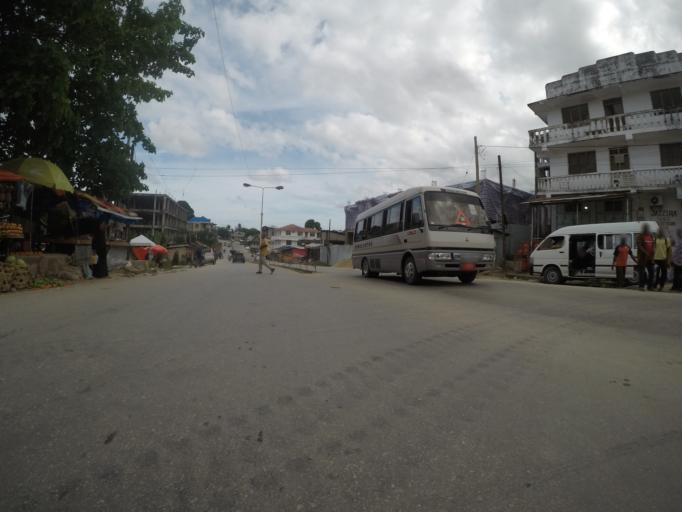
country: TZ
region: Pemba South
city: Chake Chake
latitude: -5.2470
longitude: 39.7694
